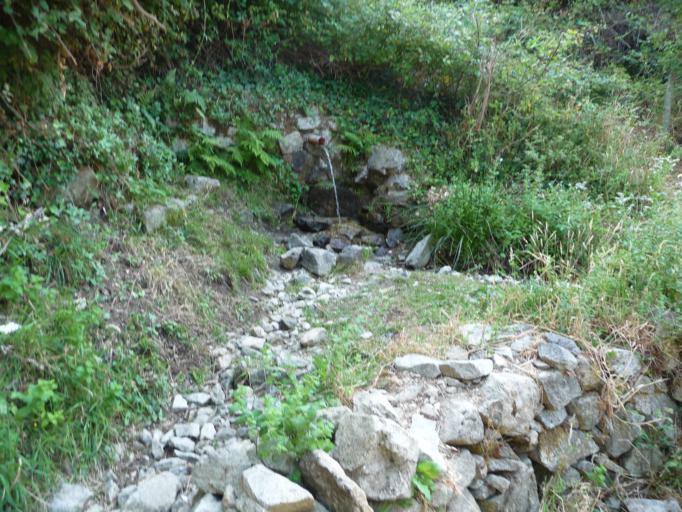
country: IT
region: Calabria
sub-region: Provincia di Reggio Calabria
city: Bivongi
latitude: 38.4893
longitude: 16.4074
